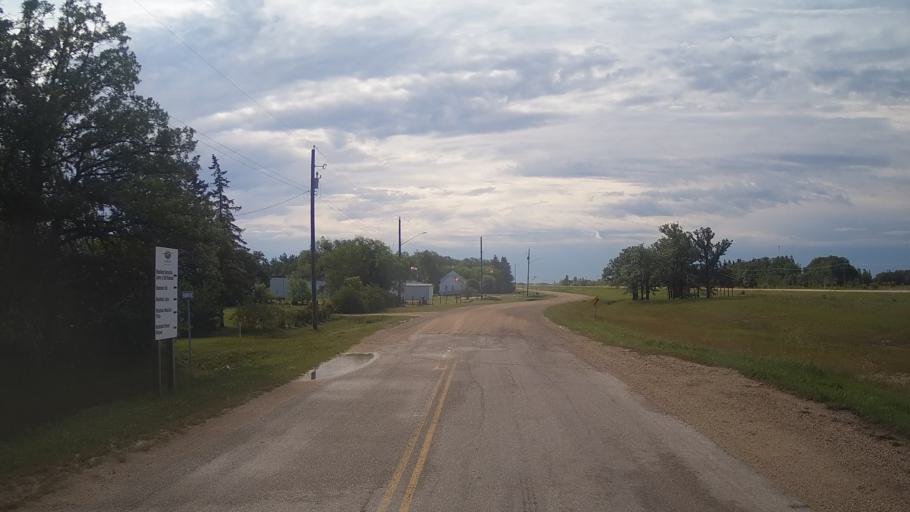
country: CA
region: Manitoba
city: Stonewall
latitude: 50.2047
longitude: -97.6571
